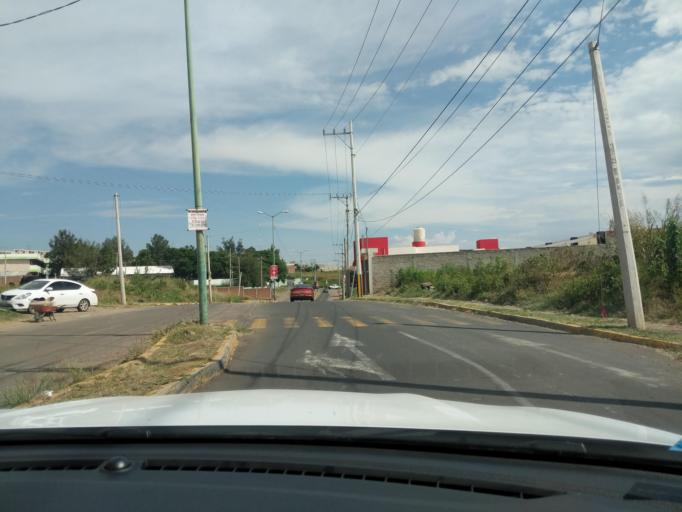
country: MX
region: Jalisco
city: San Jose del Castillo
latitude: 20.5268
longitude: -103.2348
